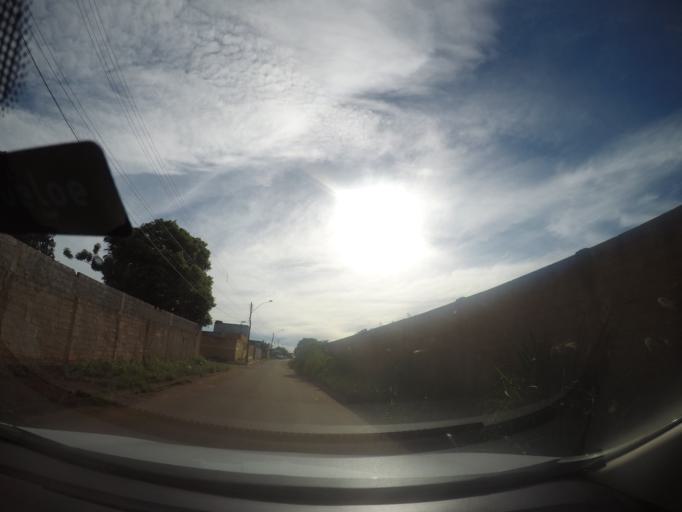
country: BR
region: Goias
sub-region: Goiania
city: Goiania
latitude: -16.6311
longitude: -49.3516
